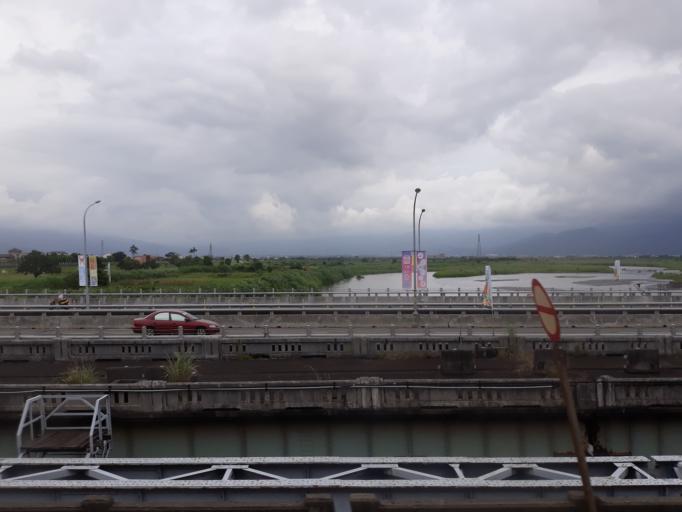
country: TW
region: Taiwan
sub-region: Yilan
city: Yilan
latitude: 24.7136
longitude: 121.7726
